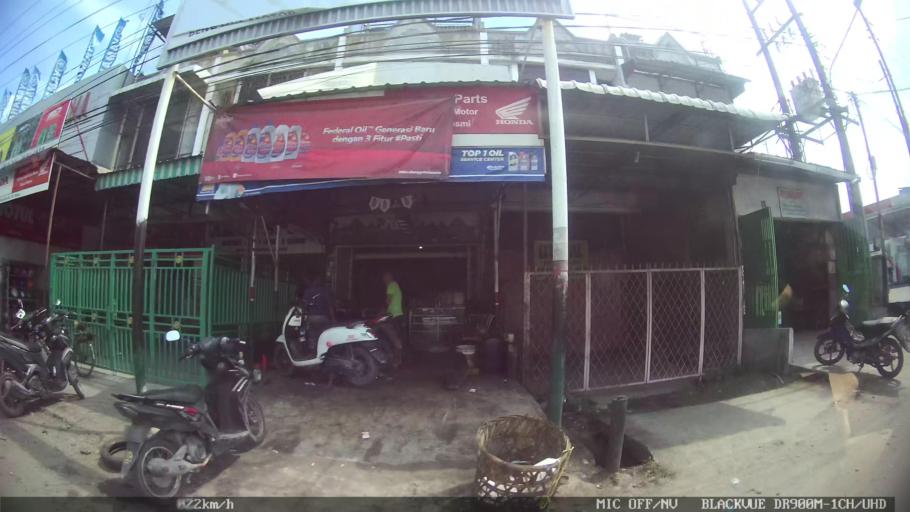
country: ID
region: North Sumatra
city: Labuhan Deli
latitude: 3.6879
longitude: 98.6629
